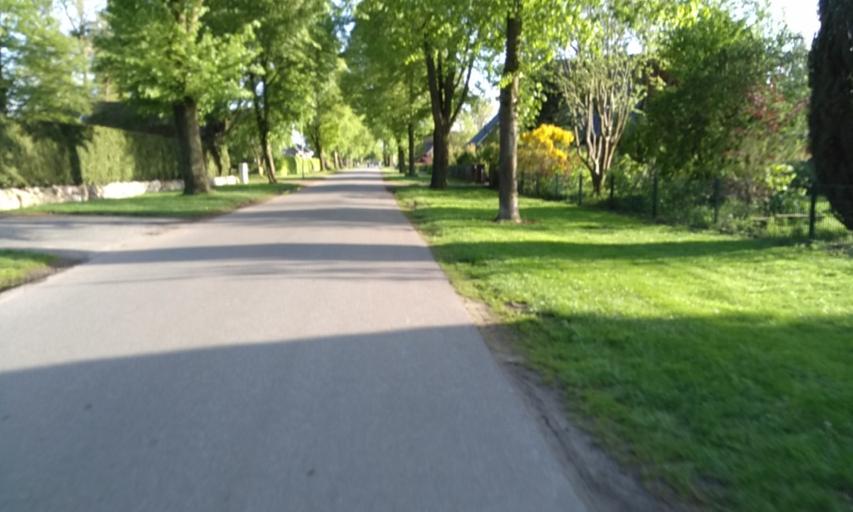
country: DE
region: Lower Saxony
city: Harsefeld
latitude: 53.4180
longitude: 9.5510
